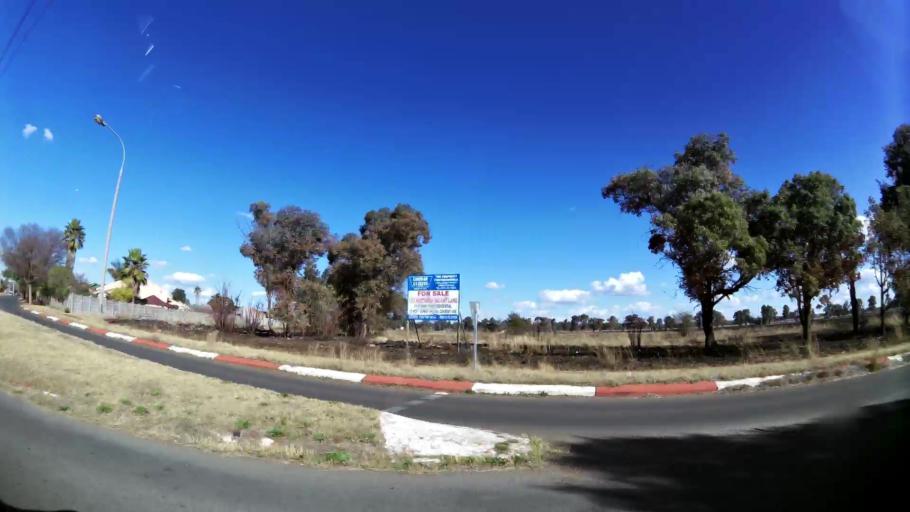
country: ZA
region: Gauteng
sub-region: West Rand District Municipality
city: Carletonville
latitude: -26.3637
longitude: 27.3760
